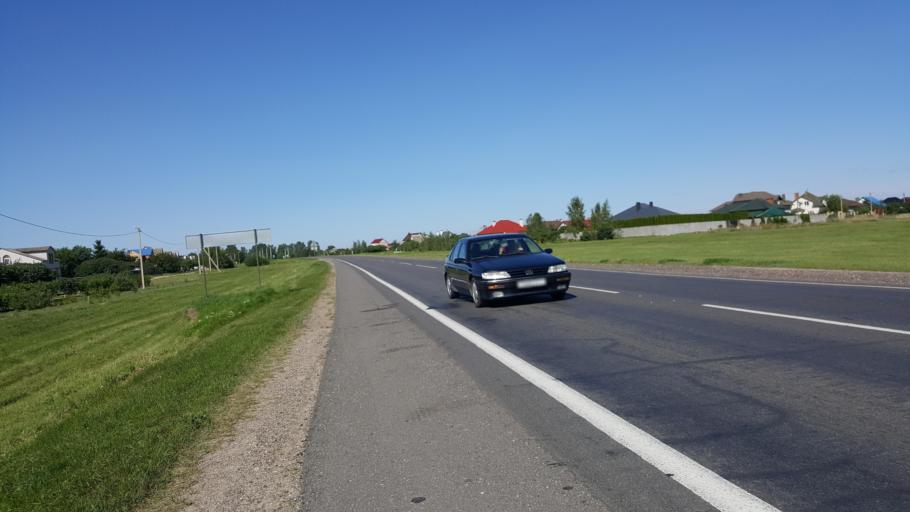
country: BY
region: Brest
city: Charnawchytsy
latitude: 52.2051
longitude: 23.7406
